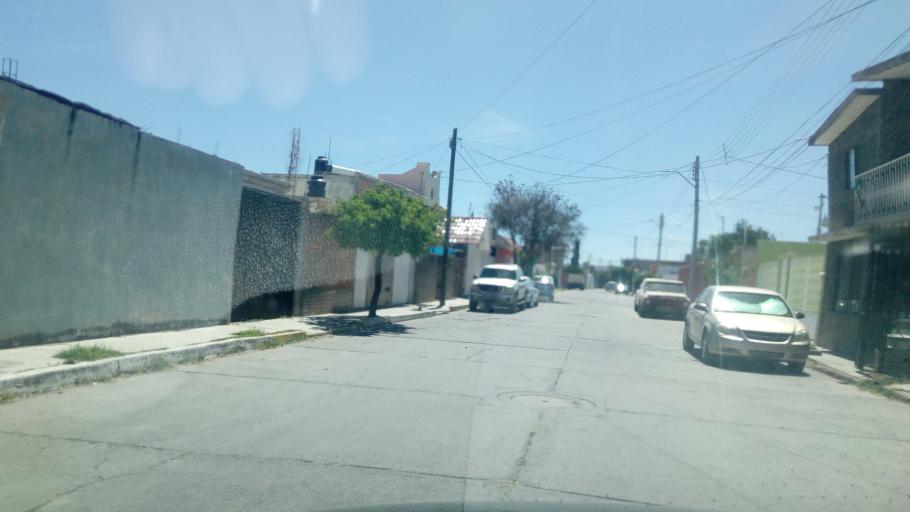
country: MX
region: Durango
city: Victoria de Durango
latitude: 24.0118
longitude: -104.6561
